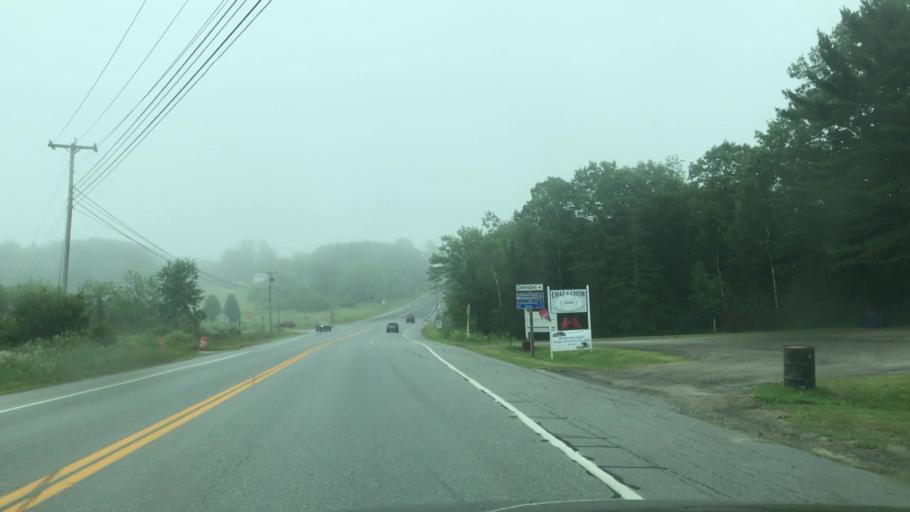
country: US
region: Maine
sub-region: Knox County
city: Warren
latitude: 44.1169
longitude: -69.2653
